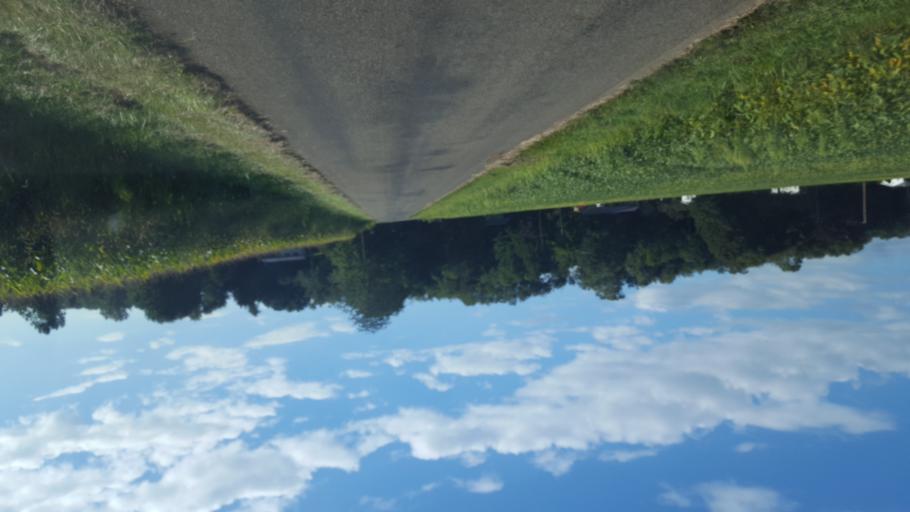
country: US
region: Ohio
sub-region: Knox County
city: Fredericktown
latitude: 40.4265
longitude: -82.5699
